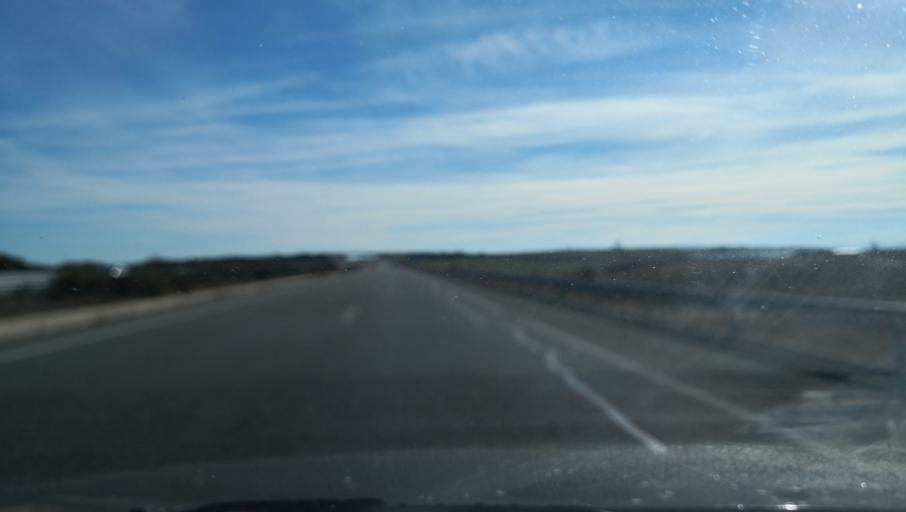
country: ES
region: Castille and Leon
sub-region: Provincia de Salamanca
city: Cantaracillo
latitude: 40.8980
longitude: -5.1676
